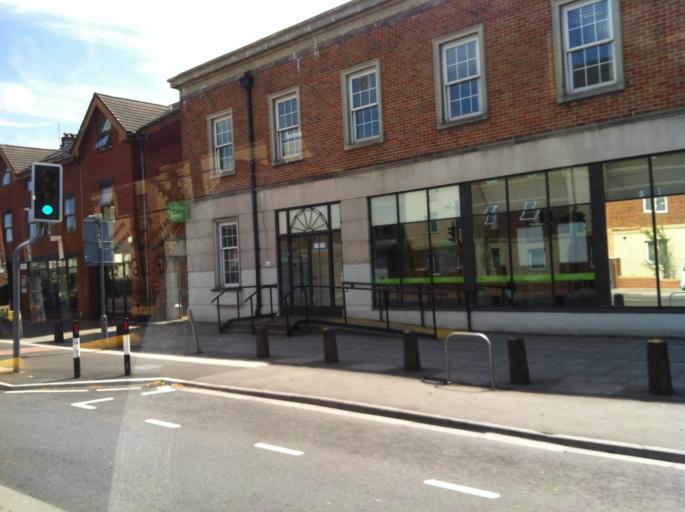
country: GB
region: Wales
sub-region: Cardiff
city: Cardiff
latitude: 51.4823
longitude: -3.2086
